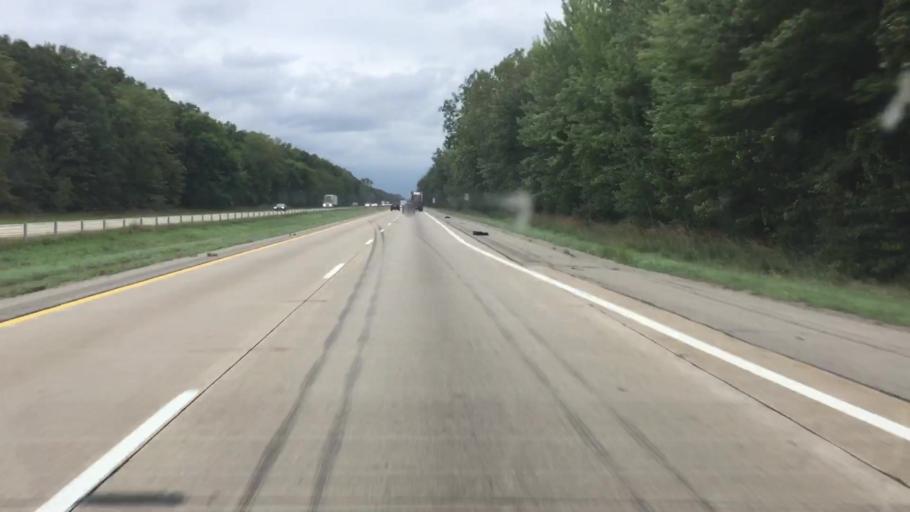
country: US
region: Michigan
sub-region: Monroe County
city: Petersburg
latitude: 41.9040
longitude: -83.6619
